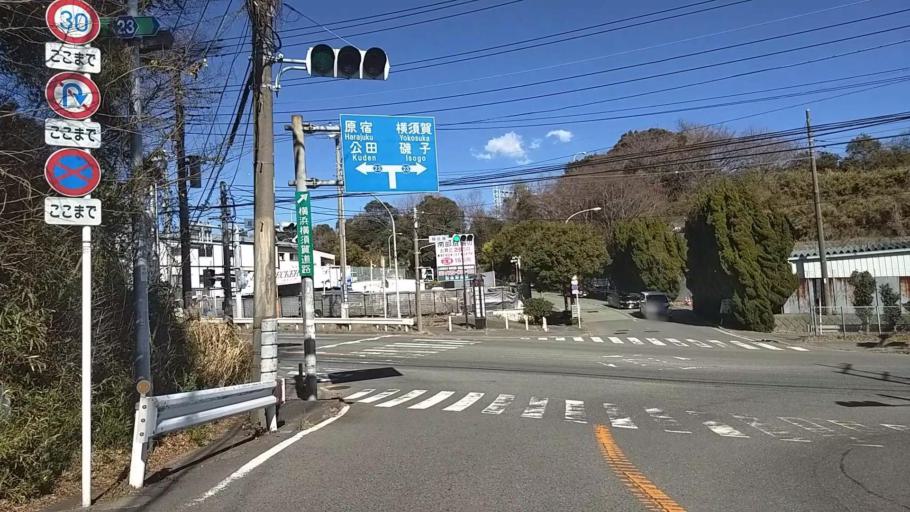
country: JP
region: Kanagawa
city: Zushi
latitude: 35.3327
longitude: 139.5914
